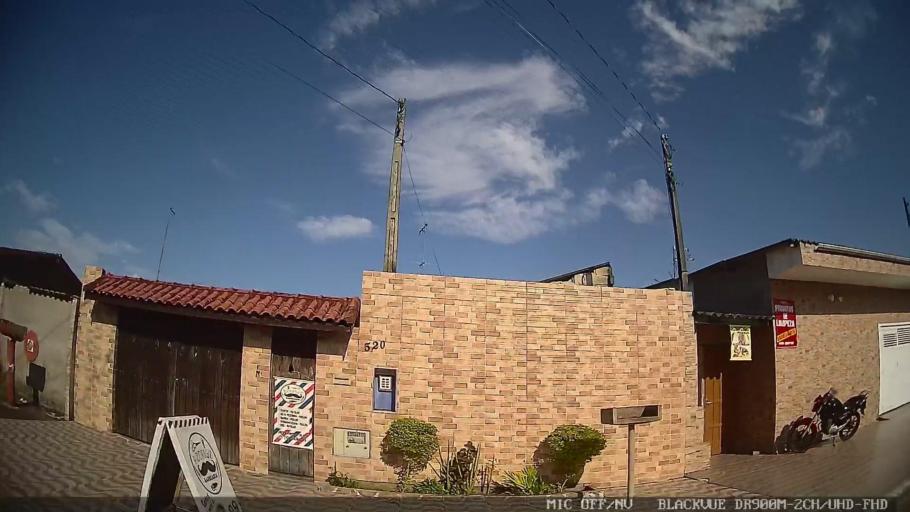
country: BR
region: Sao Paulo
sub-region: Itanhaem
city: Itanhaem
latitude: -24.1771
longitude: -46.8188
